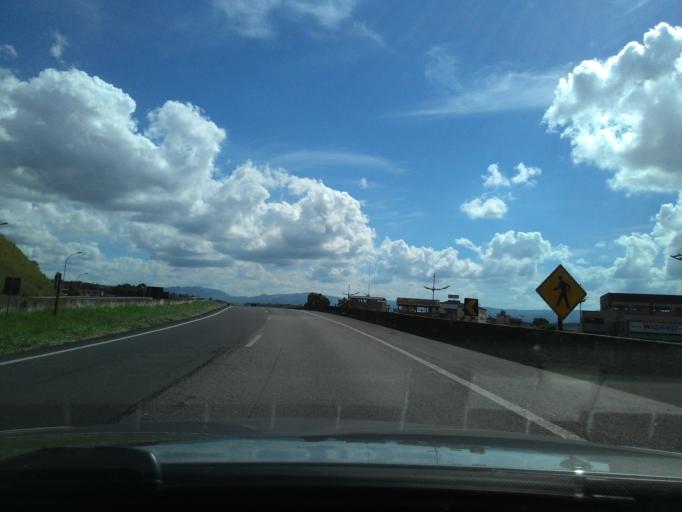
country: BR
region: Sao Paulo
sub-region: Cajati
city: Cajati
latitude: -24.7301
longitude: -48.1076
